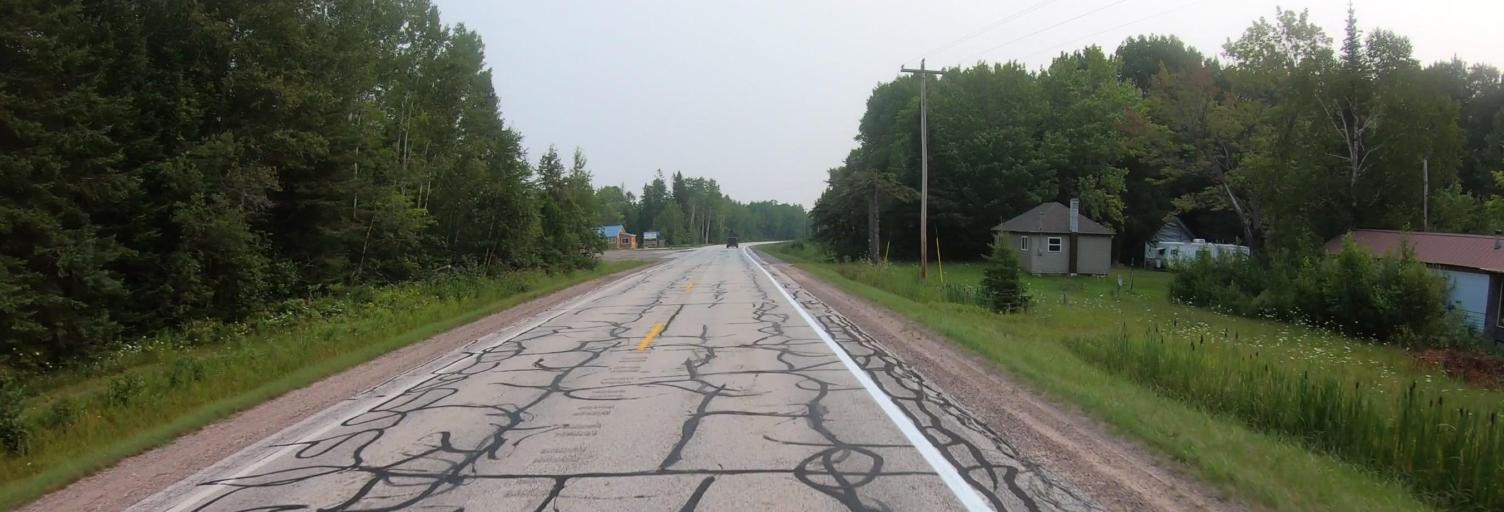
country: US
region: Michigan
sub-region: Luce County
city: Newberry
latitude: 46.5072
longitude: -85.0922
